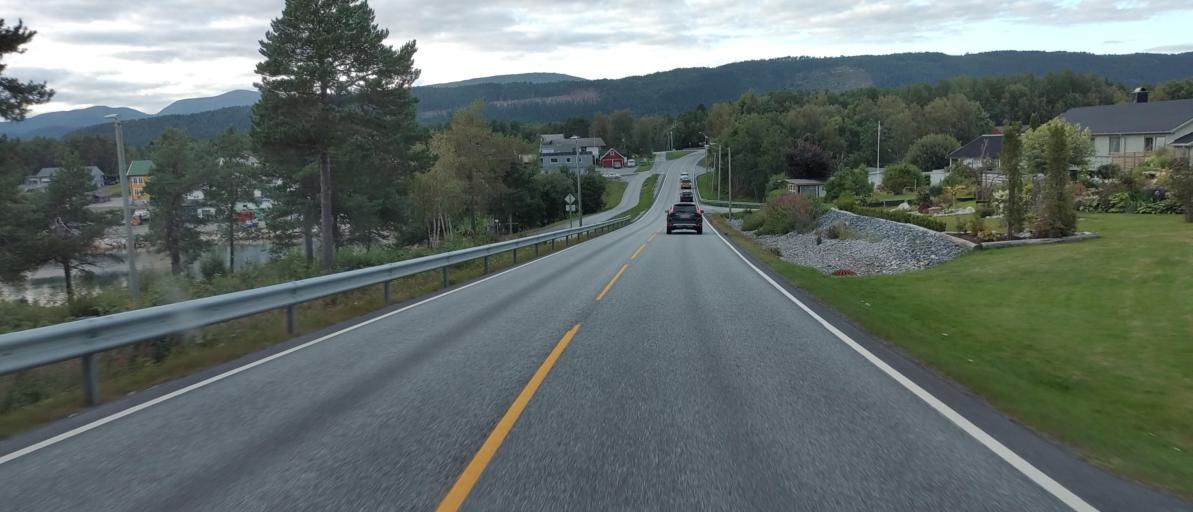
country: NO
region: More og Romsdal
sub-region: Molde
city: Hjelset
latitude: 62.7158
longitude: 7.4279
